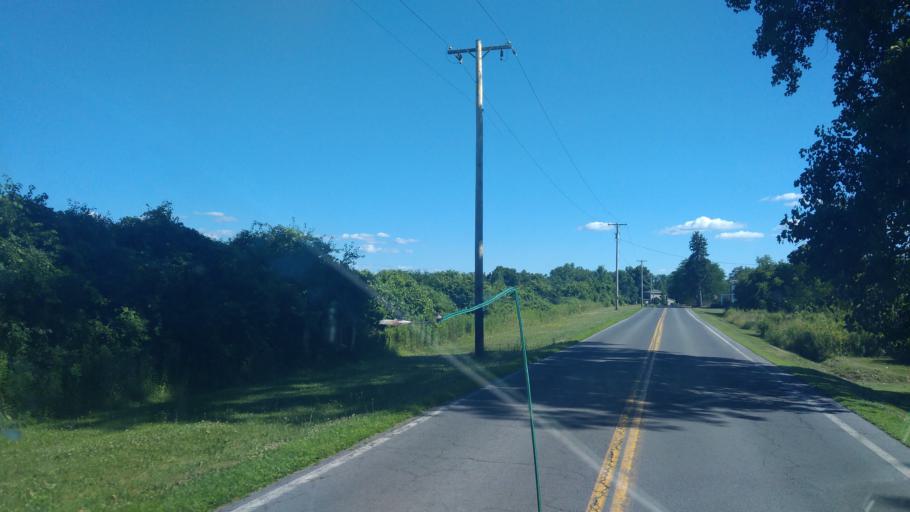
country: US
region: New York
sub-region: Seneca County
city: Seneca Falls
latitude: 42.9966
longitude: -76.8067
